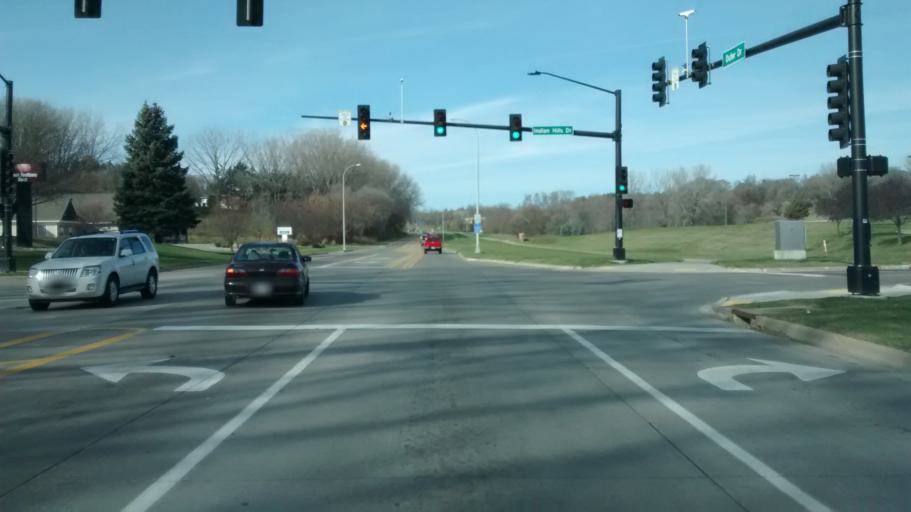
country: US
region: Iowa
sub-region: Woodbury County
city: Sioux City
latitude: 42.5367
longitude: -96.3742
